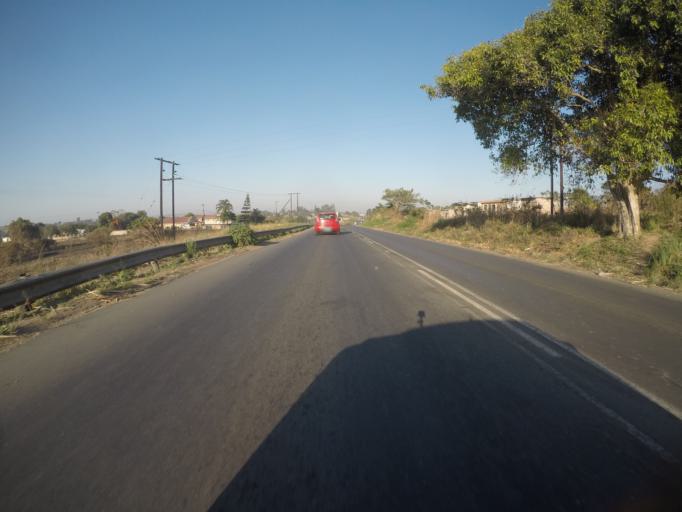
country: ZA
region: KwaZulu-Natal
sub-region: iLembe District Municipality
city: Stanger
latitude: -29.4096
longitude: 31.2464
